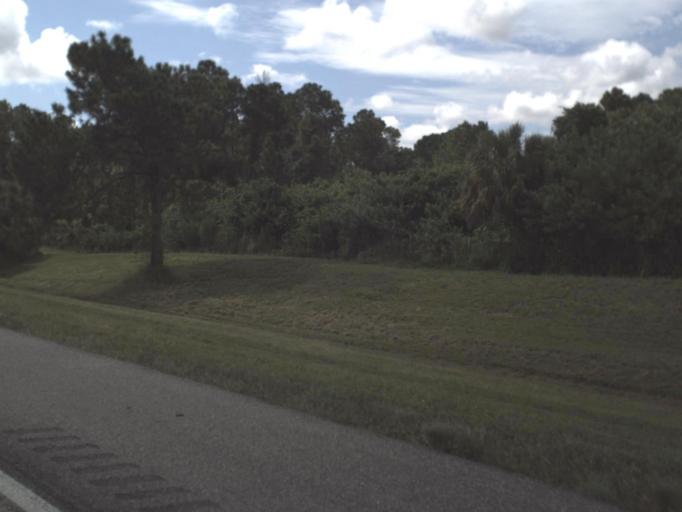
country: US
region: Florida
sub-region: Charlotte County
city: Port Charlotte
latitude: 27.0756
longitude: -82.1028
